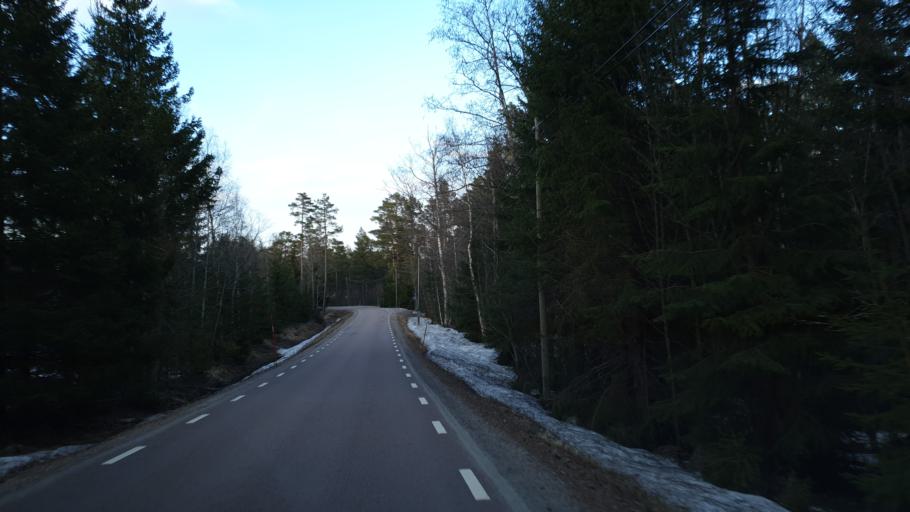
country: SE
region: Vaesternorrland
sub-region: Sundsvalls Kommun
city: Njurundabommen
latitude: 62.2378
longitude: 17.5209
